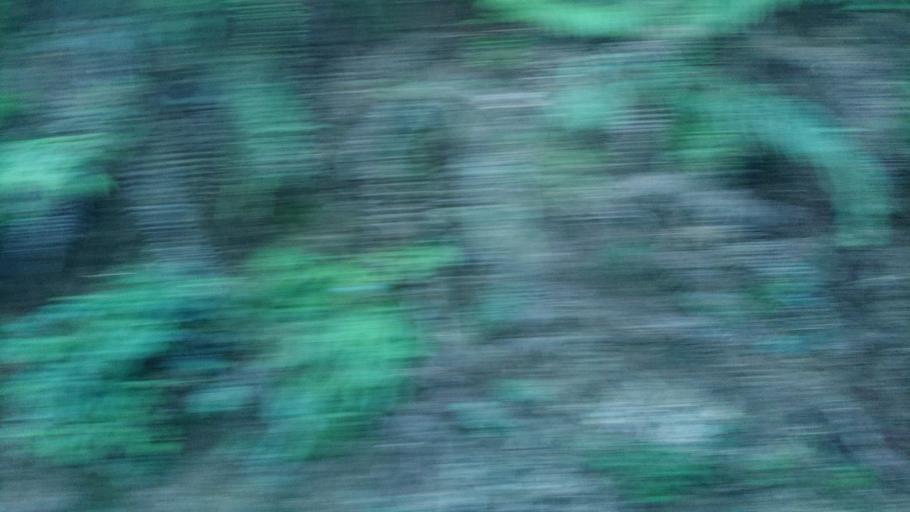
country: TW
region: Taiwan
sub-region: Chiayi
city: Jiayi Shi
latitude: 23.5348
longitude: 120.6391
